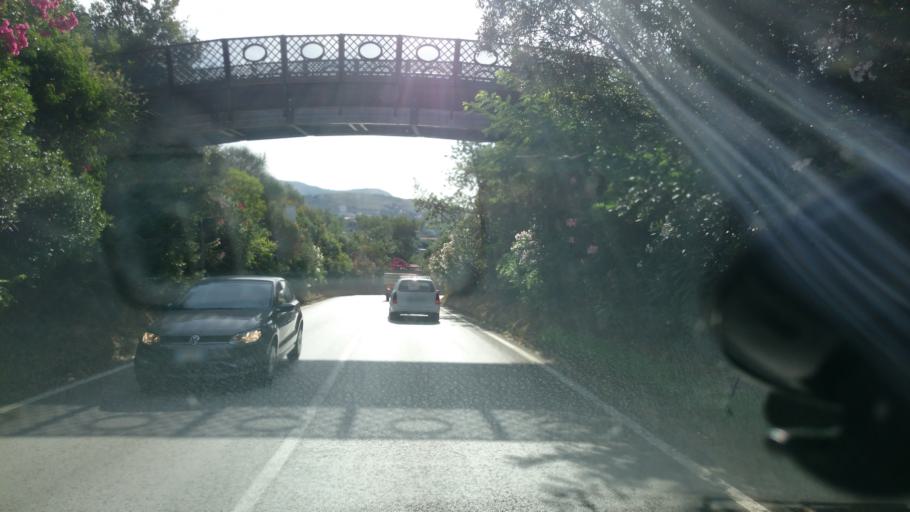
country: IT
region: Campania
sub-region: Provincia di Salerno
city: Marina di Camerota
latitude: 40.0067
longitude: 15.3546
